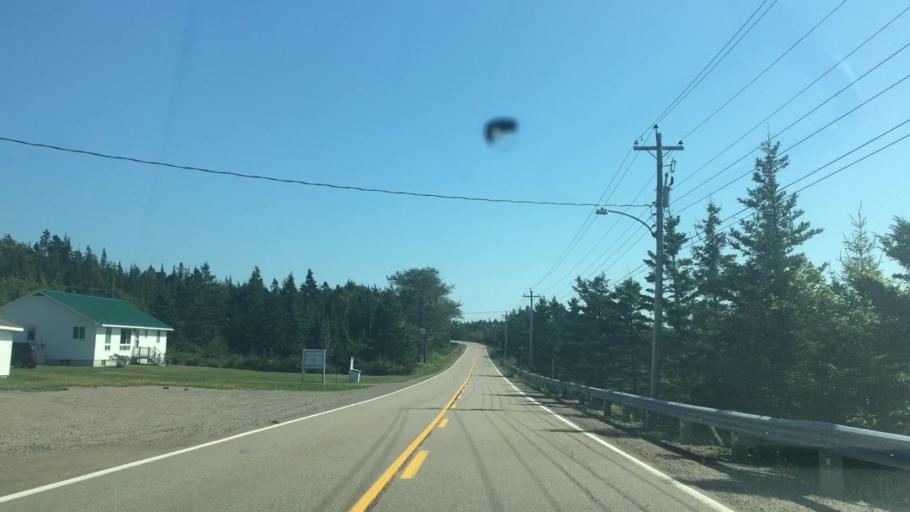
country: CA
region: Nova Scotia
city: Antigonish
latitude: 45.0221
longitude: -62.0123
